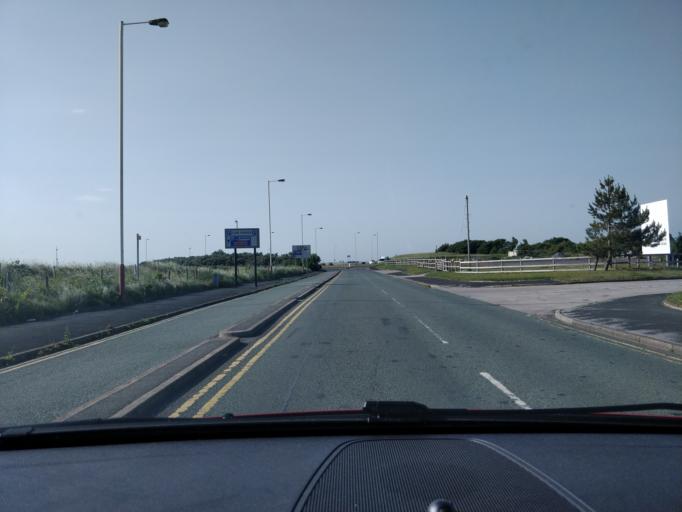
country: GB
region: England
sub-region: Sefton
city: Southport
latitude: 53.6609
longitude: -2.9981
